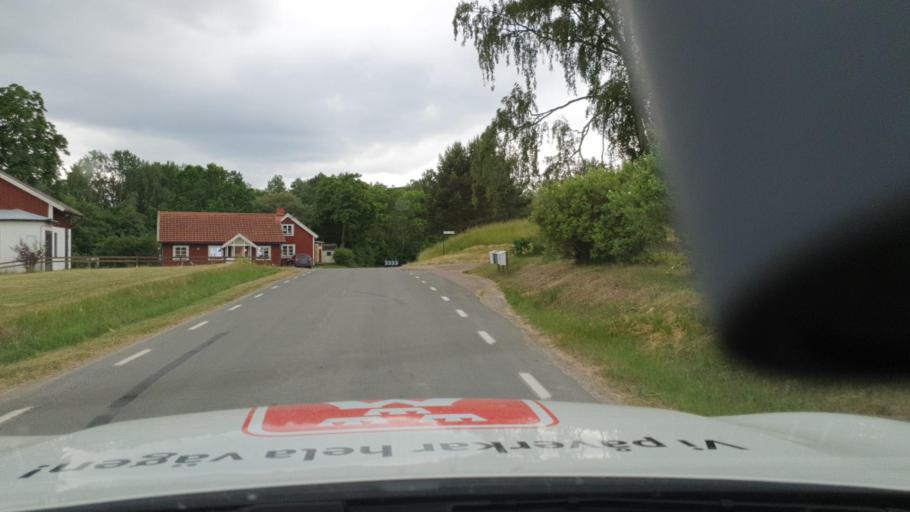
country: SE
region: Vaestra Goetaland
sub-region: Hjo Kommun
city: Hjo
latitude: 58.1771
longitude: 14.1941
